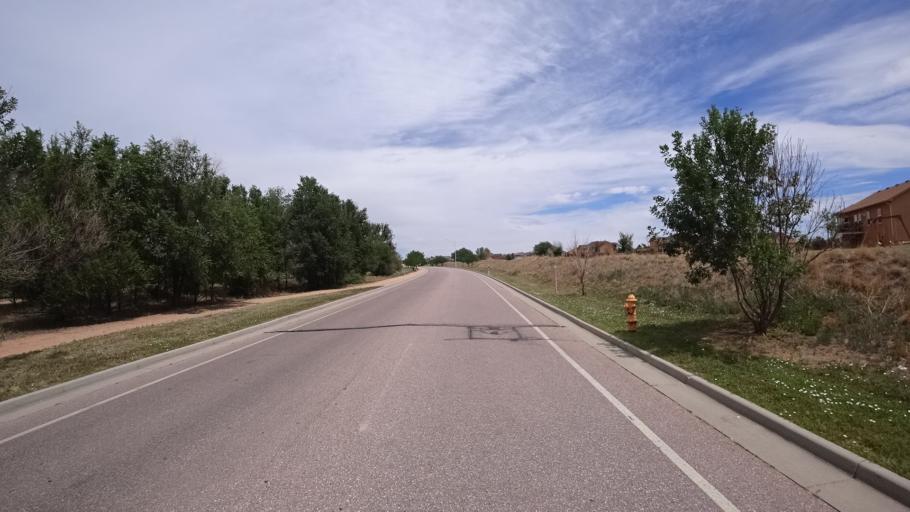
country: US
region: Colorado
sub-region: El Paso County
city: Fountain
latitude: 38.6864
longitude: -104.6864
